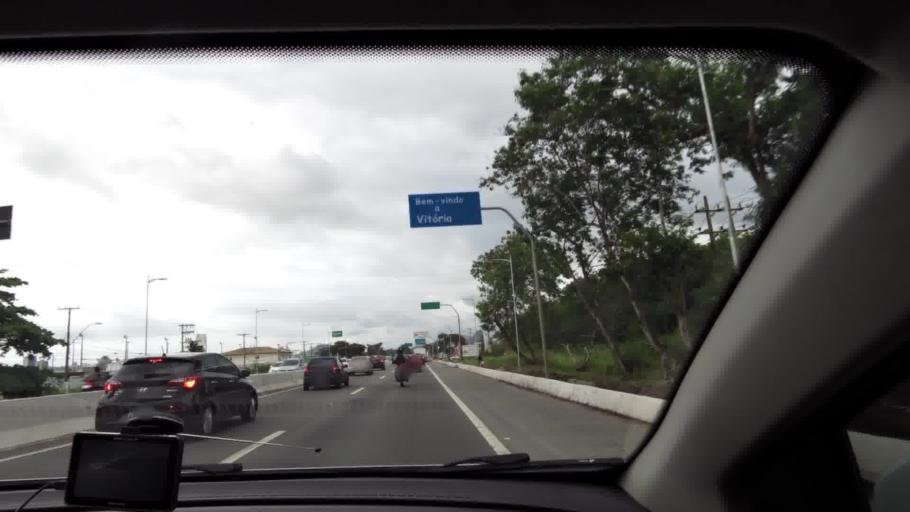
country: BR
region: Espirito Santo
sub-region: Vila Velha
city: Vila Velha
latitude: -20.2535
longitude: -40.2884
